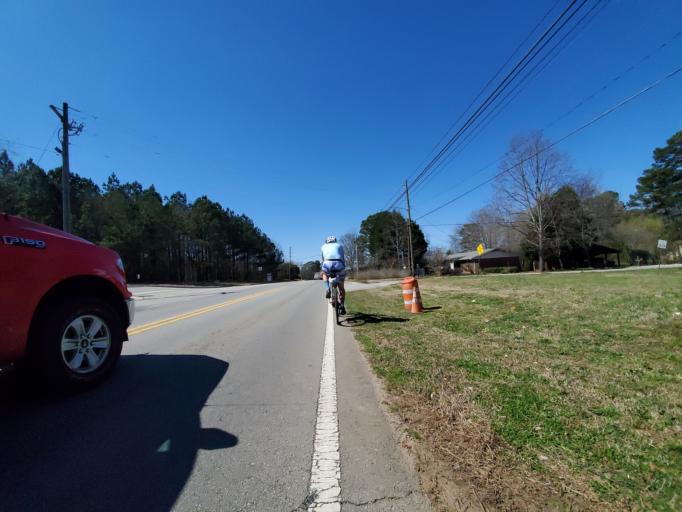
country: US
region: Georgia
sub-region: Barrow County
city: Russell
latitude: 33.9981
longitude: -83.6985
